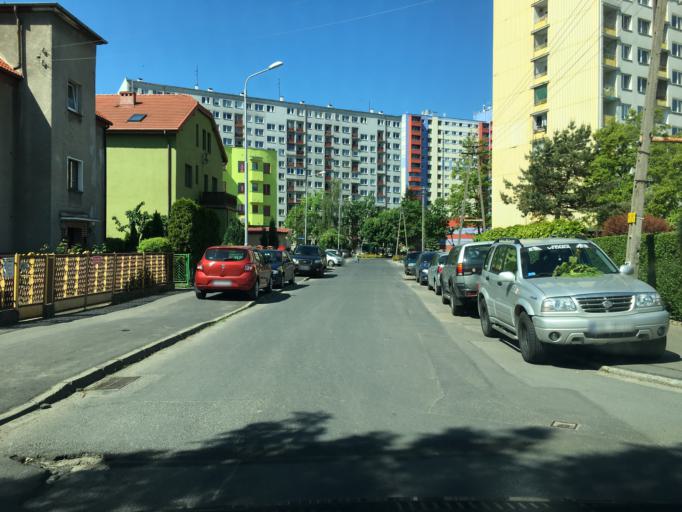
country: PL
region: Lower Silesian Voivodeship
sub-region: Powiat wroclawski
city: Wroclaw
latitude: 51.1115
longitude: 16.9627
